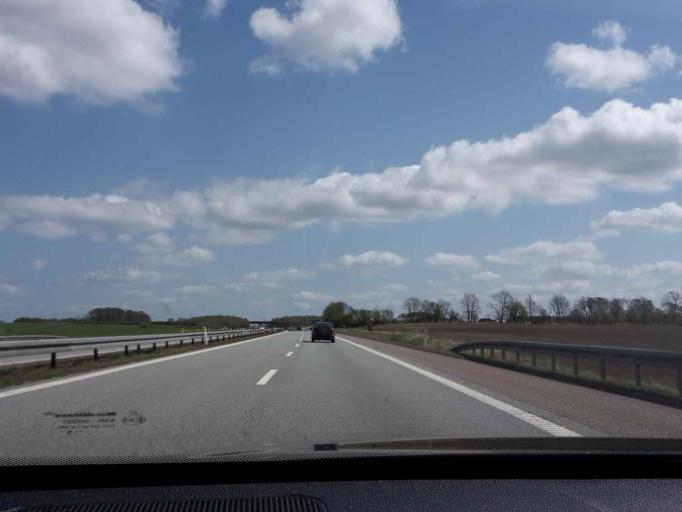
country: DK
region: South Denmark
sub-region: Vejen Kommune
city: Brorup
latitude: 55.5060
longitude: 9.0081
